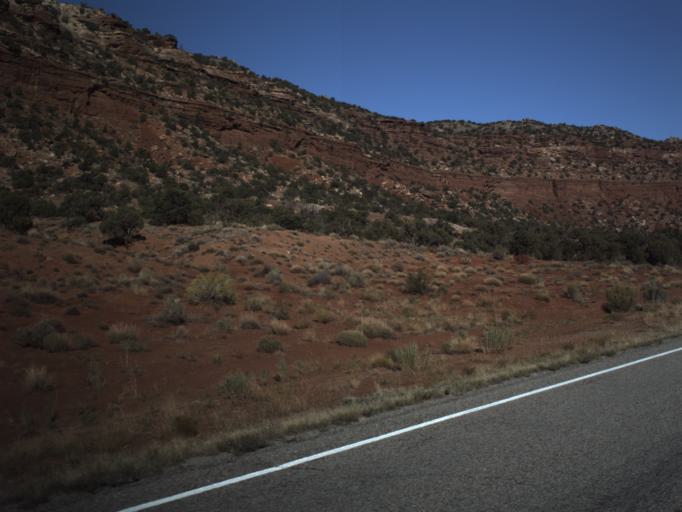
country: US
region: Utah
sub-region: San Juan County
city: Blanding
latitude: 37.6111
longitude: -110.0810
